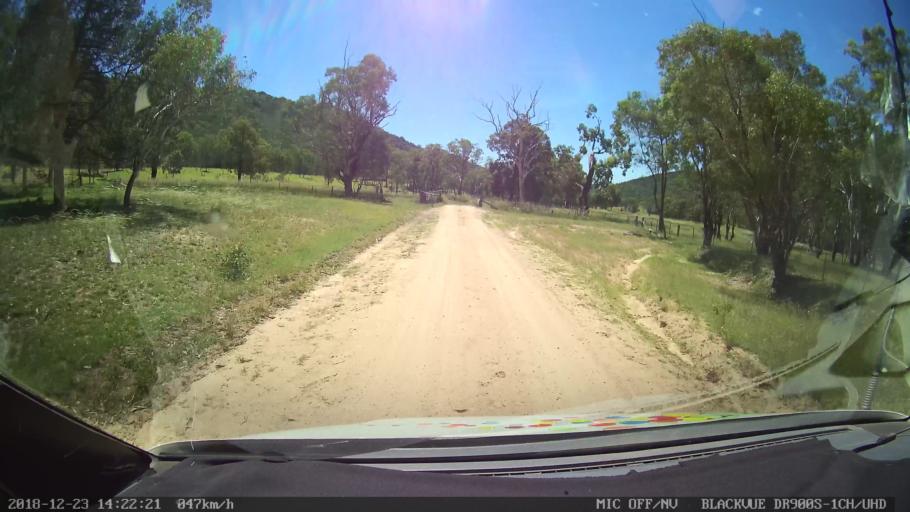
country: AU
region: New South Wales
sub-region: Tamworth Municipality
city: Manilla
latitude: -30.6419
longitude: 150.9737
